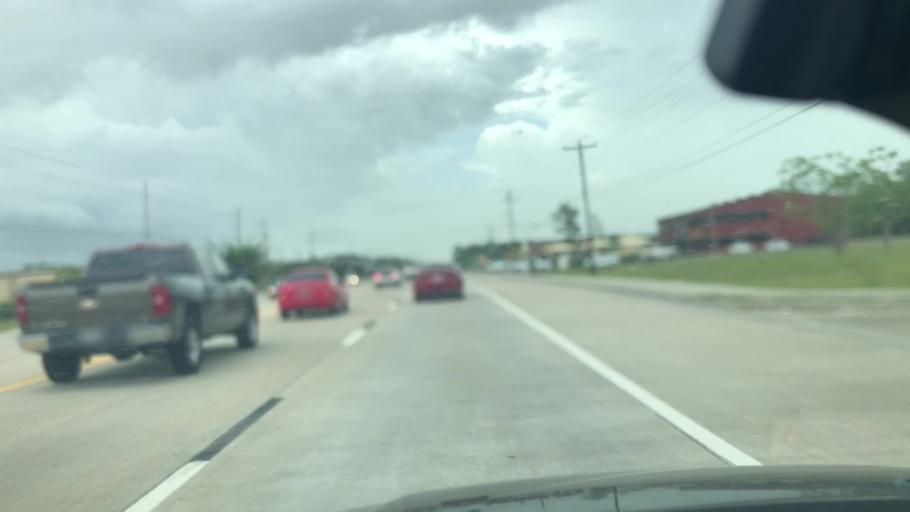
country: US
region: Texas
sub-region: Galveston County
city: Dickinson
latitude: 29.4723
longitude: -95.0812
